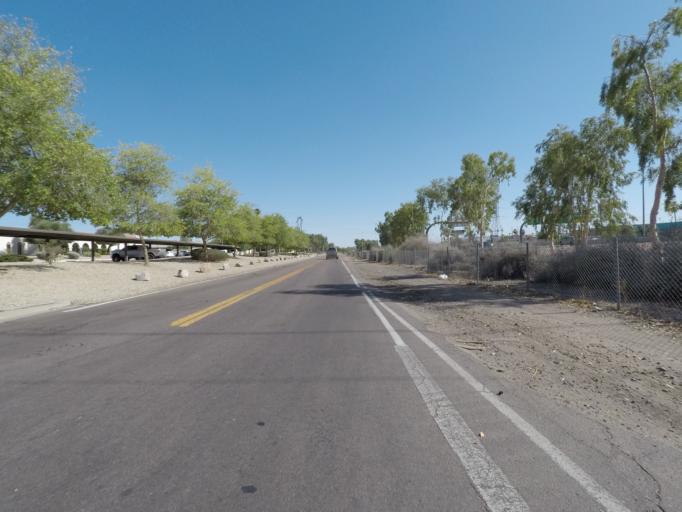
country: US
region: Arizona
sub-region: Maricopa County
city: Tempe Junction
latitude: 33.4279
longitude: -111.9775
